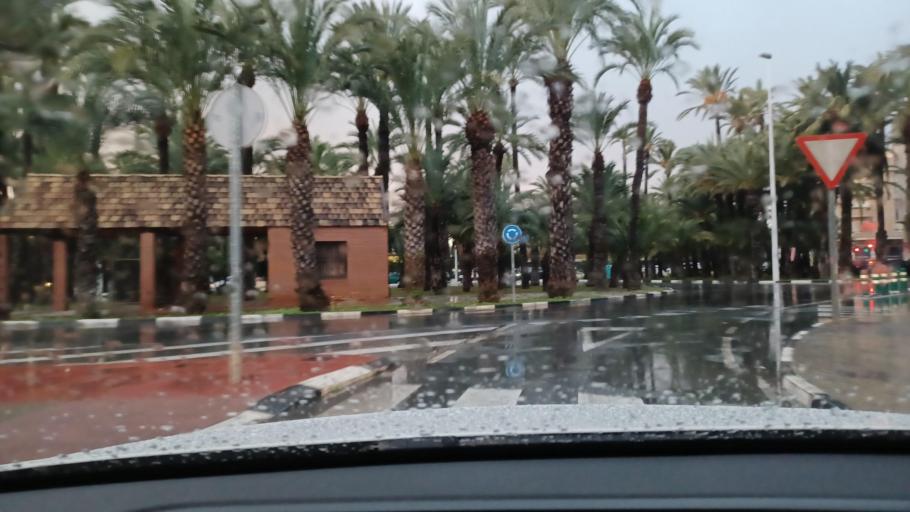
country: ES
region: Valencia
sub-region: Provincia de Alicante
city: Elche
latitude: 38.2578
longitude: -0.6930
